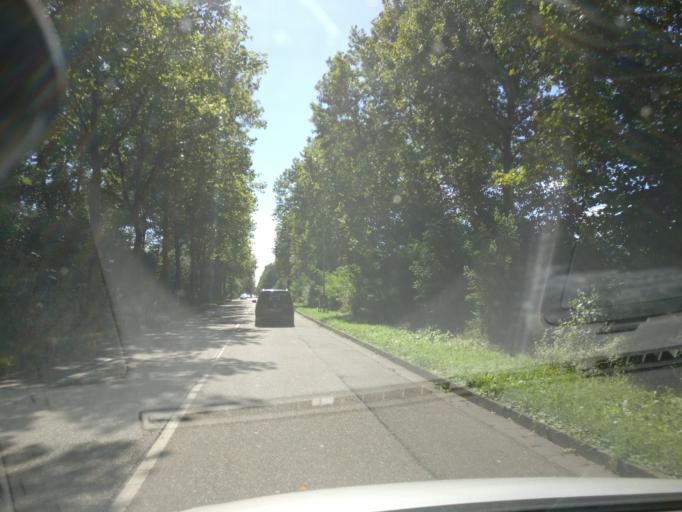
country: DE
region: Baden-Wuerttemberg
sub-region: Karlsruhe Region
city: Ettlingen
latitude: 48.9247
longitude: 8.3649
